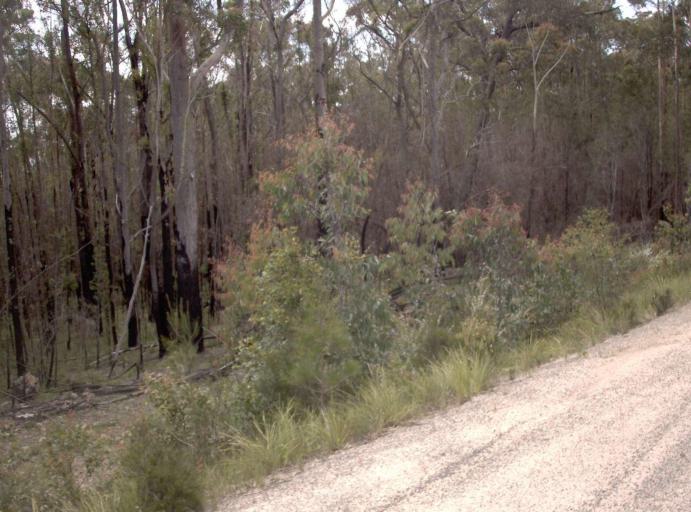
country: AU
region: New South Wales
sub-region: Bega Valley
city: Eden
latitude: -37.5398
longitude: 149.4639
